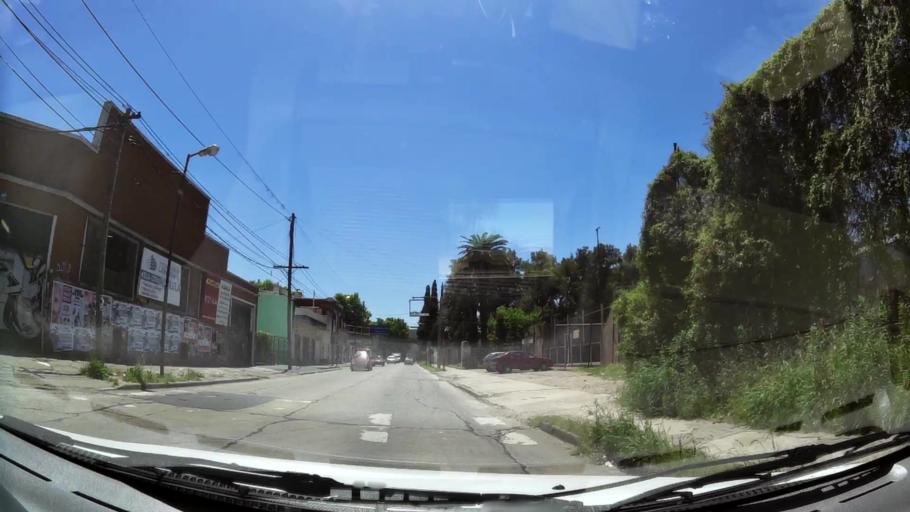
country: AR
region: Buenos Aires
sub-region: Partido de General San Martin
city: General San Martin
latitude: -34.5560
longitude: -58.5335
